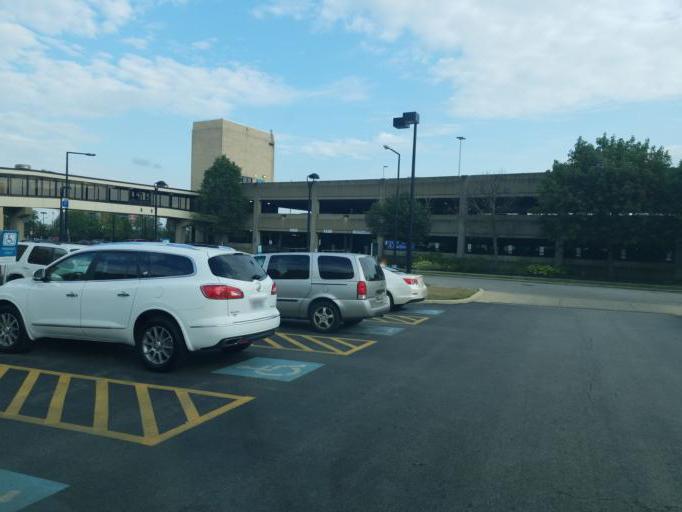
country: US
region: Ohio
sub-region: Mahoning County
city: Youngstown
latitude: 41.1136
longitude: -80.6580
